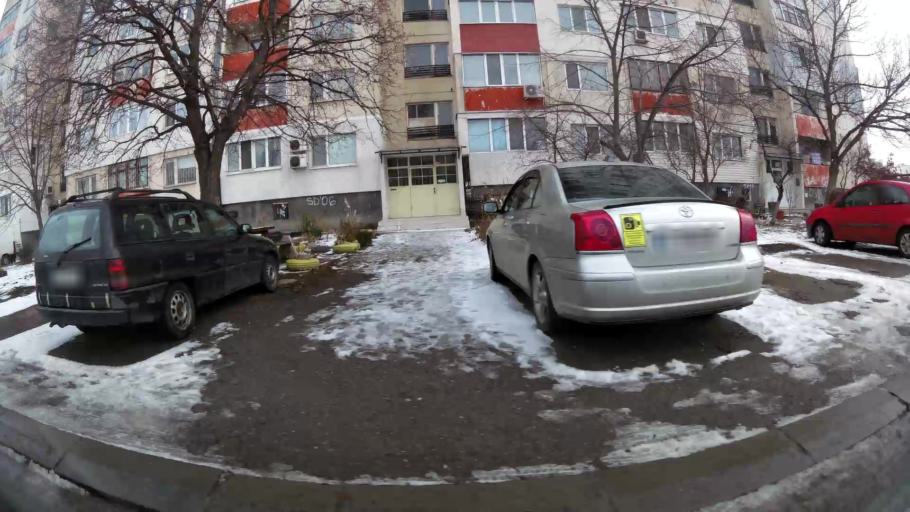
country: BG
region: Sofia-Capital
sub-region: Stolichna Obshtina
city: Sofia
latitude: 42.7112
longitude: 23.3756
